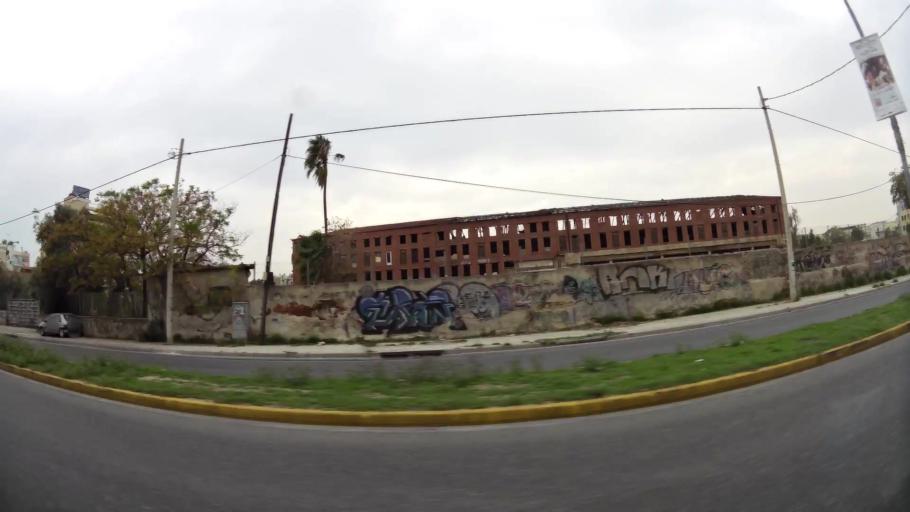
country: GR
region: Attica
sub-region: Nomos Piraios
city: Agios Ioannis Rentis
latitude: 37.9702
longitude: 23.6640
